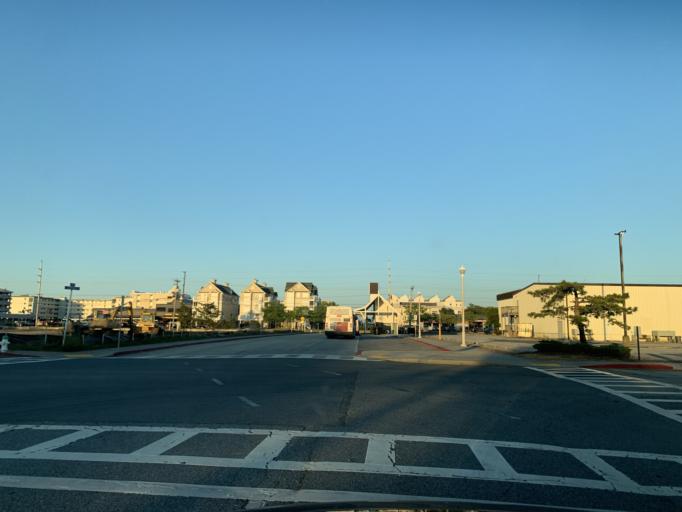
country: US
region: Delaware
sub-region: Sussex County
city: Bethany Beach
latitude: 38.4495
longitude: -75.0543
